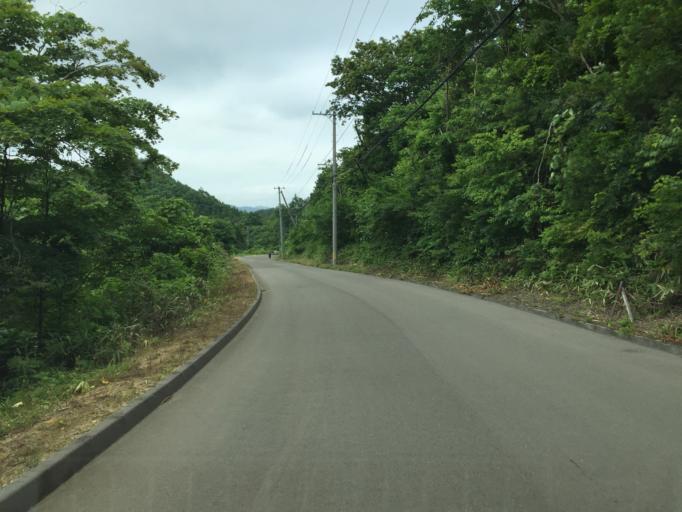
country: JP
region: Miyagi
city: Marumori
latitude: 37.8086
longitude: 140.7410
